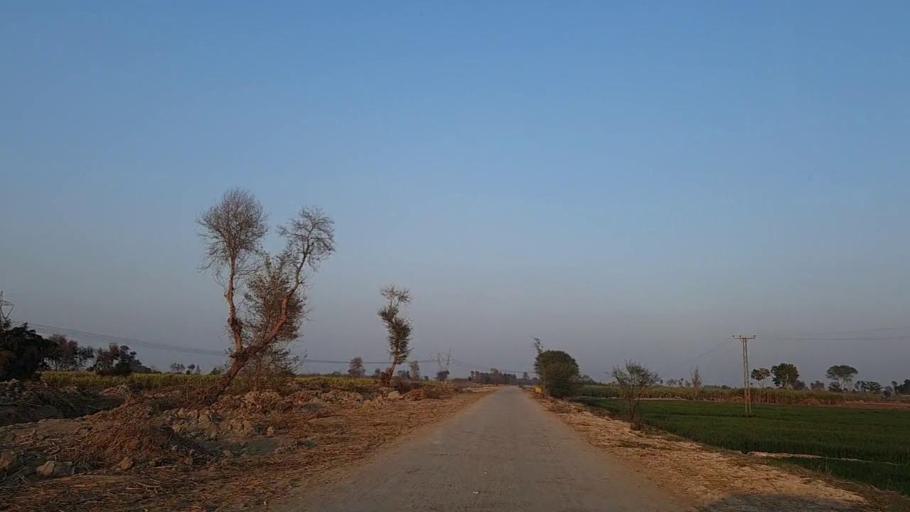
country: PK
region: Sindh
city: Moro
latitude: 26.7632
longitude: 68.0424
